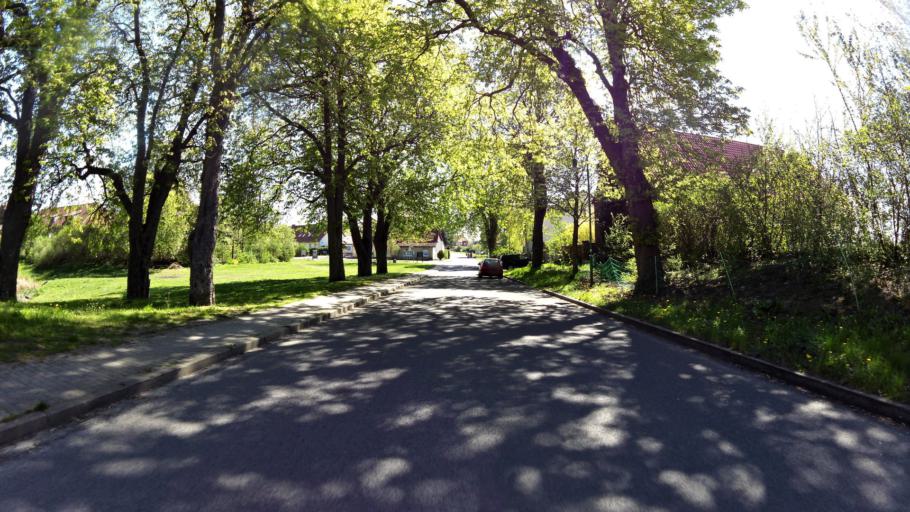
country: DE
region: Brandenburg
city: Werftpfuhl
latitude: 52.6385
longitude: 13.7956
